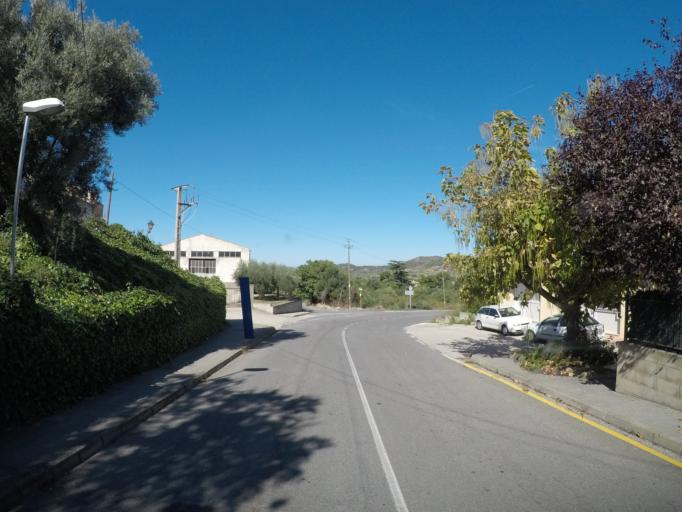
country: ES
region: Catalonia
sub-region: Provincia de Tarragona
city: Falset
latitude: 41.1471
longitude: 0.8199
